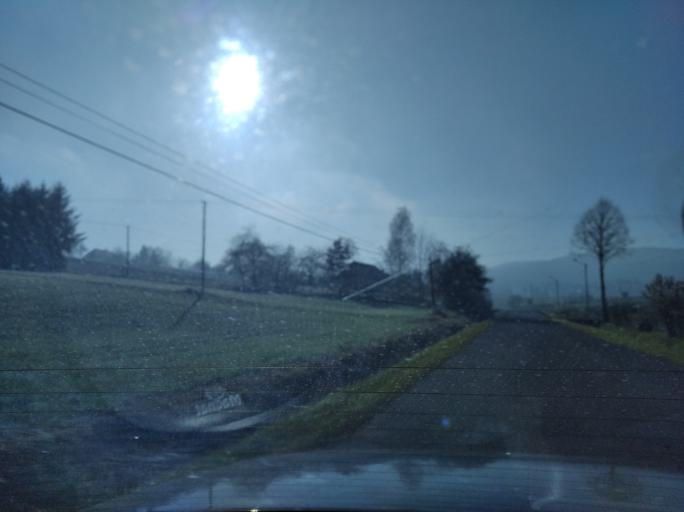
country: PL
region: Subcarpathian Voivodeship
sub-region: Powiat strzyzowski
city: Wysoka Strzyzowska
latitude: 49.8508
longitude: 21.7012
